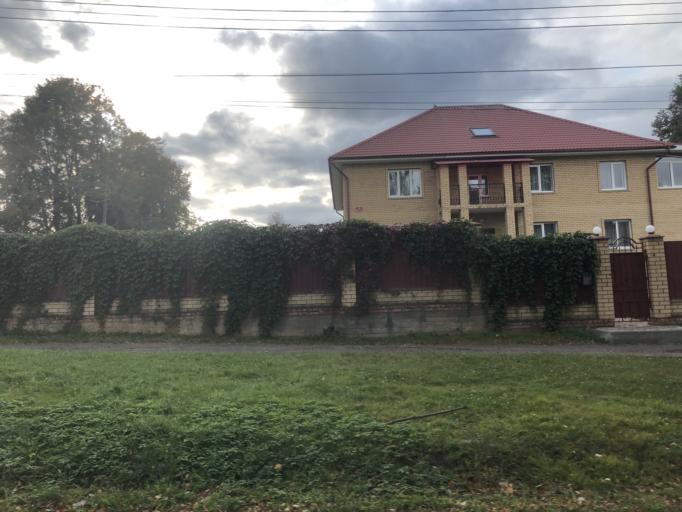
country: RU
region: Tverskaya
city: Rzhev
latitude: 56.2551
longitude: 34.2930
